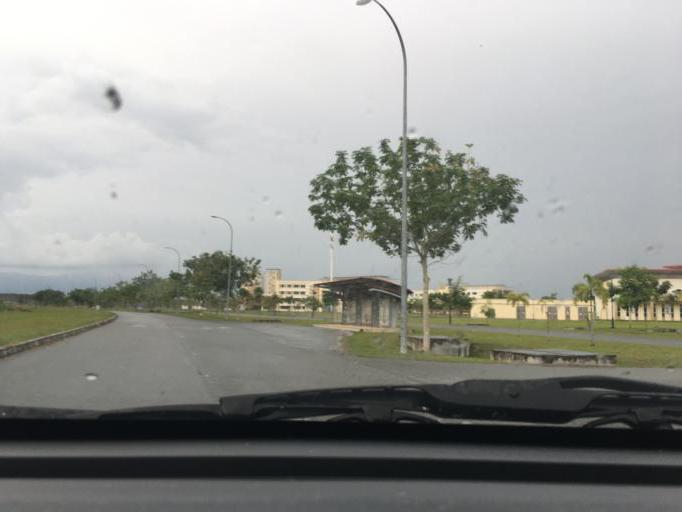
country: MY
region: Kedah
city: Sungai Petani
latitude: 5.5863
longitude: 100.6436
